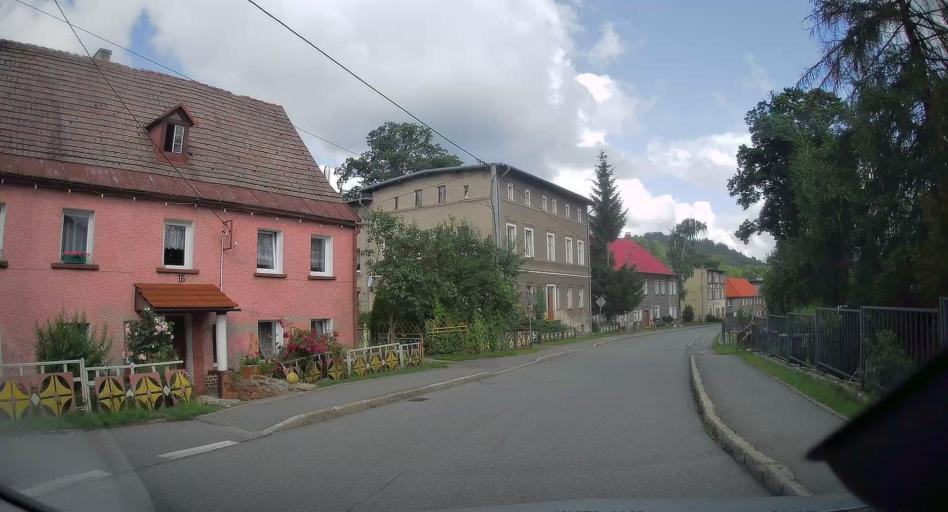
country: PL
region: Lower Silesian Voivodeship
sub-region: Powiat walbrzyski
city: Walim
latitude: 50.7008
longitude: 16.4394
